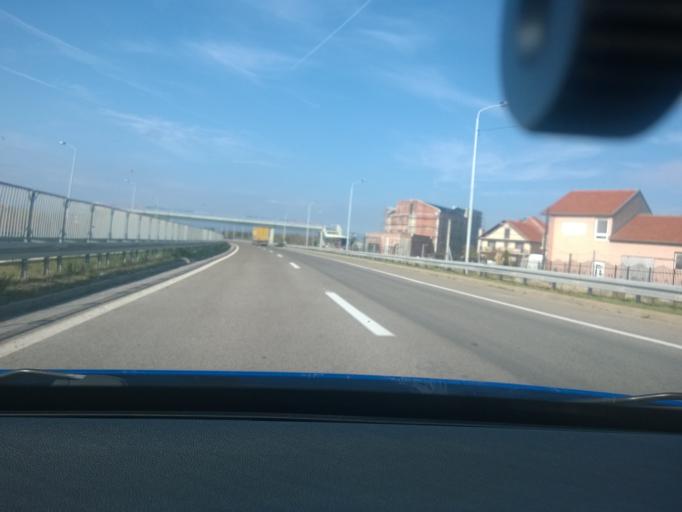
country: RS
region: Central Serbia
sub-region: Nisavski Okrug
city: Nis
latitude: 43.3465
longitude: 21.8751
